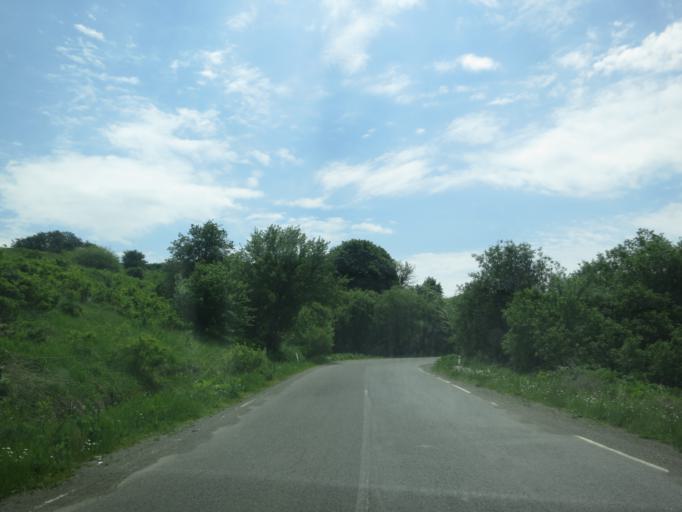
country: GE
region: Kakheti
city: Sagarejo
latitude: 41.8659
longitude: 45.2738
